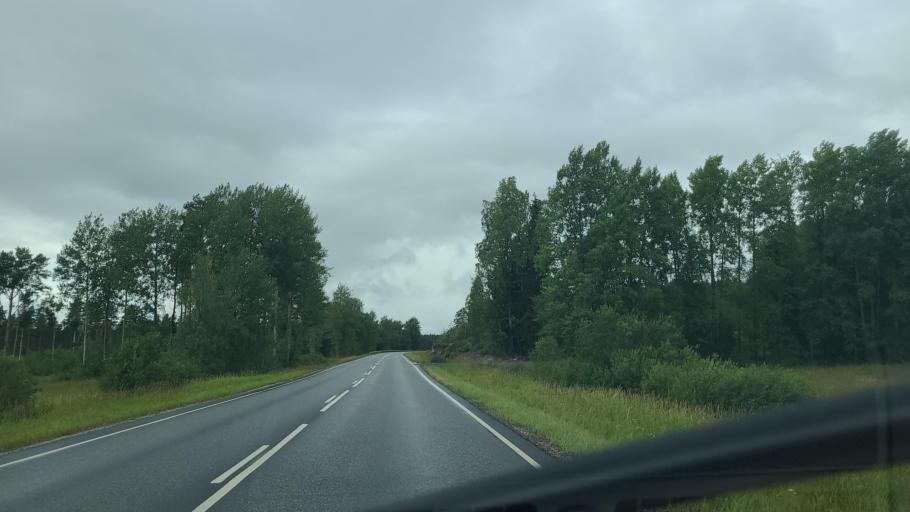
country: FI
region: Varsinais-Suomi
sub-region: Aboland-Turunmaa
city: Kimito
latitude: 60.2029
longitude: 22.6536
